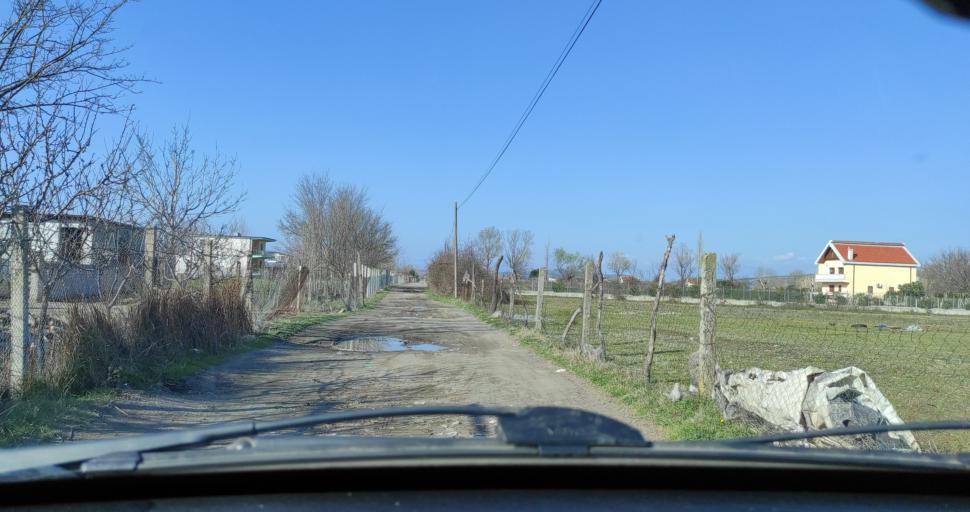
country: AL
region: Shkoder
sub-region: Rrethi i Shkodres
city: Velipoje
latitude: 41.8705
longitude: 19.4114
